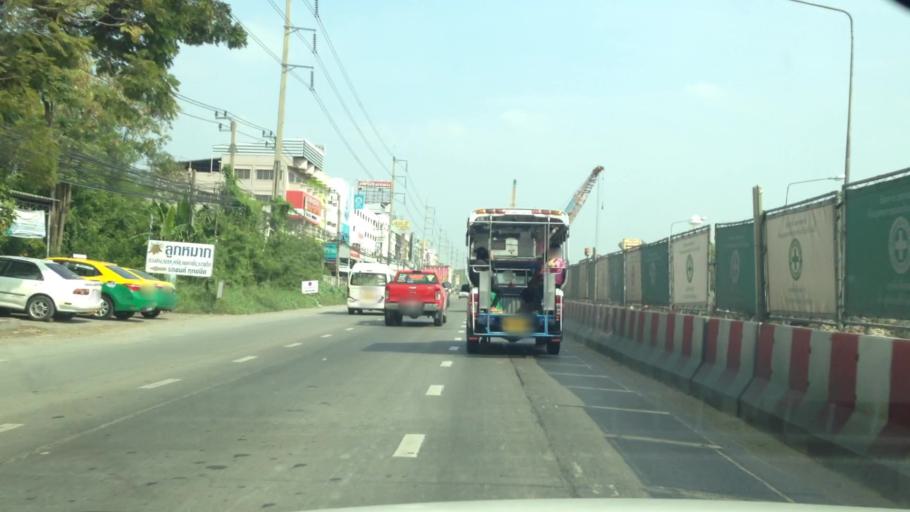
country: TH
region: Samut Prakan
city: Samut Prakan
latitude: 13.6026
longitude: 100.6134
